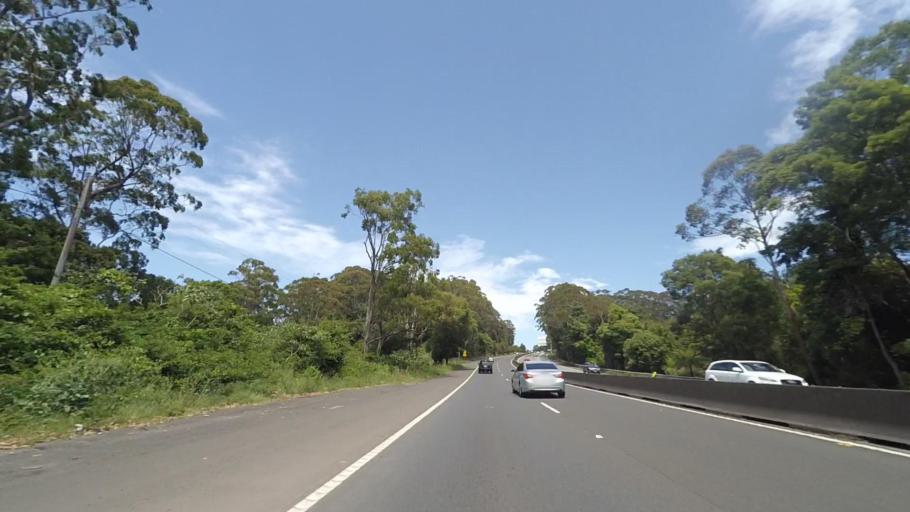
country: AU
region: New South Wales
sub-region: Wollongong
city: Bulli
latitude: -34.3152
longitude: 150.8935
